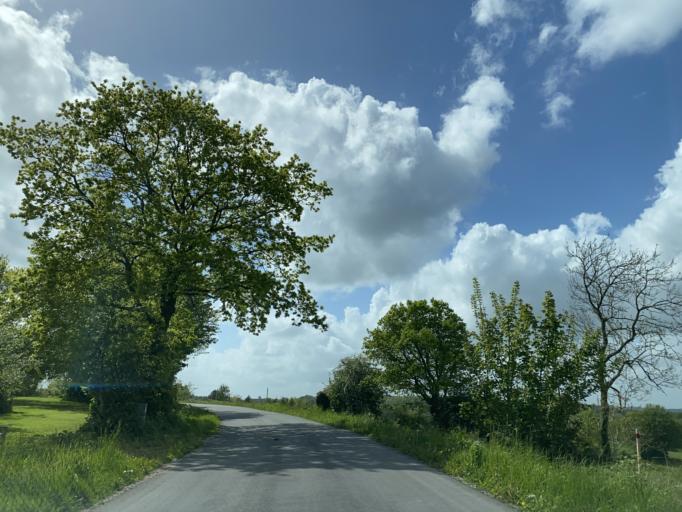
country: DK
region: South Denmark
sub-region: Aabenraa Kommune
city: Aabenraa
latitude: 55.0068
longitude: 9.4554
